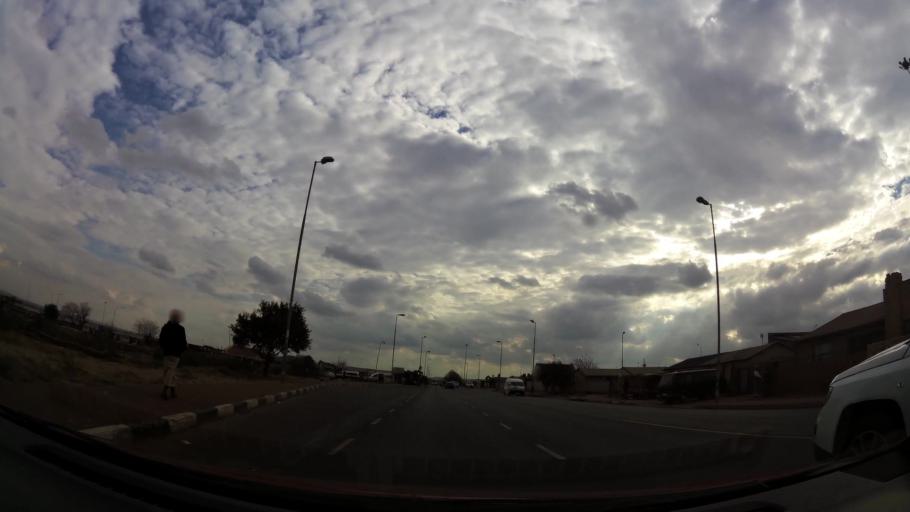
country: ZA
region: Gauteng
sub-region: City of Johannesburg Metropolitan Municipality
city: Soweto
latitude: -26.2488
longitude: 27.8191
